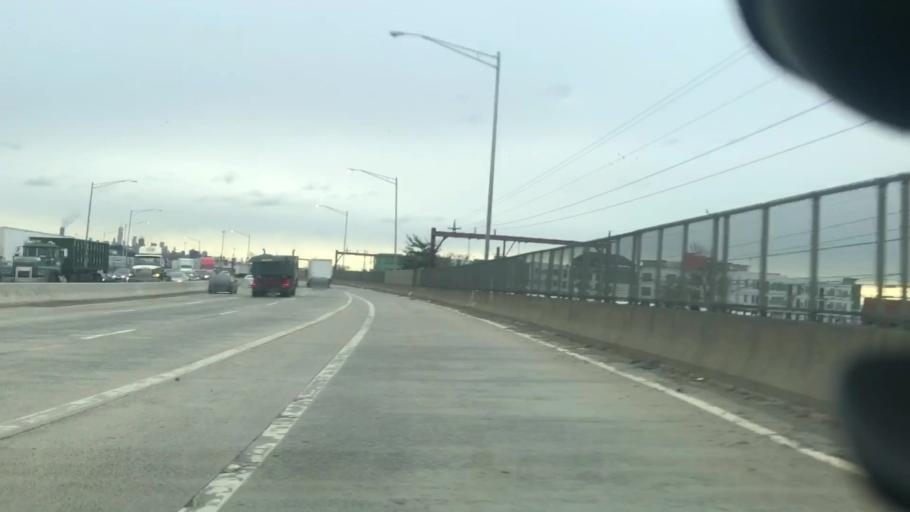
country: US
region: New Jersey
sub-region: Hudson County
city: Harrison
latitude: 40.7430
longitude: -74.1570
